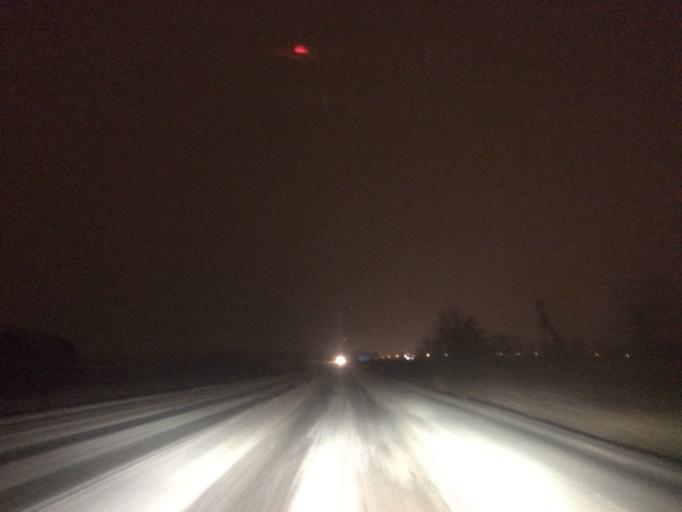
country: RU
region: Tula
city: Kosaya Gora
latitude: 54.1583
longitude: 37.4533
